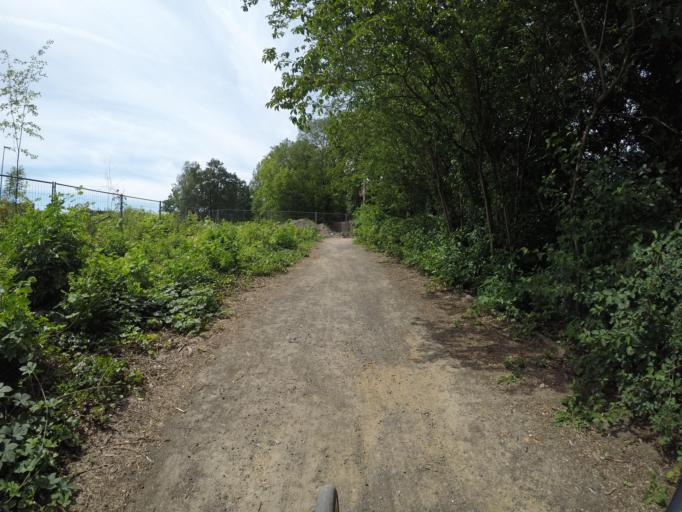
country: DE
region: Berlin
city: Kopenick Bezirk
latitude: 52.4528
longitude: 13.5649
